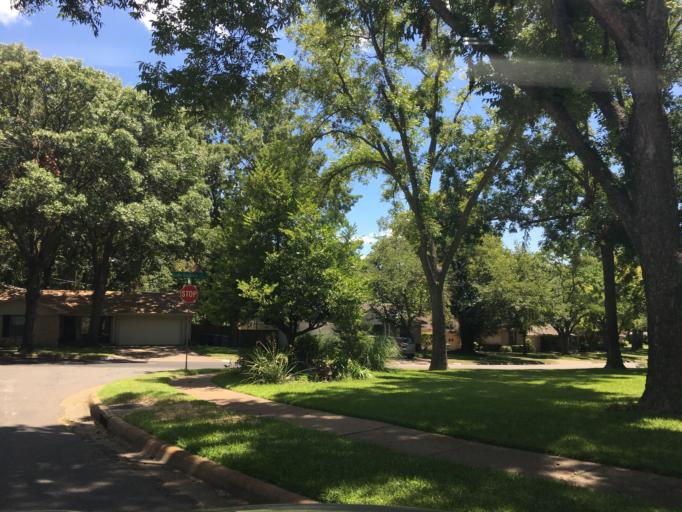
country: US
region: Texas
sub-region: Dallas County
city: Garland
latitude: 32.8473
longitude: -96.6931
